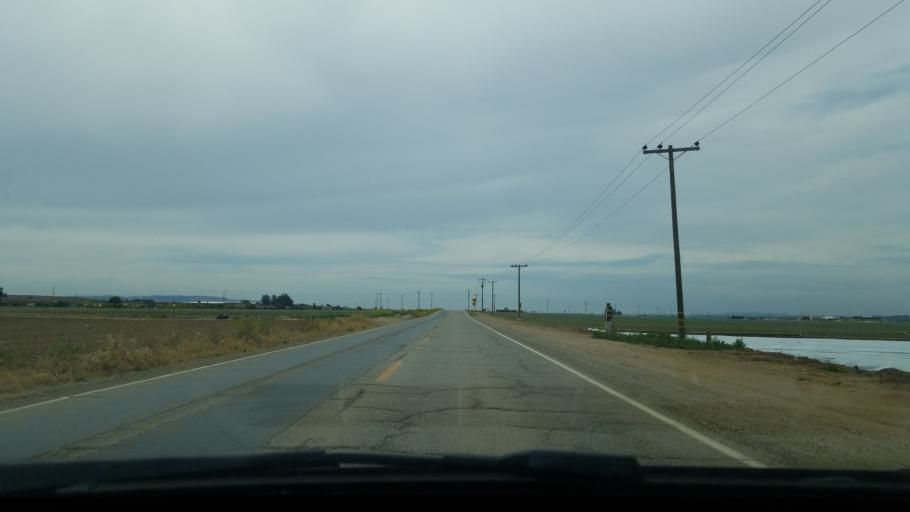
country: US
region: California
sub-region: Santa Barbara County
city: Orcutt
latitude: 34.9074
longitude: -120.3253
